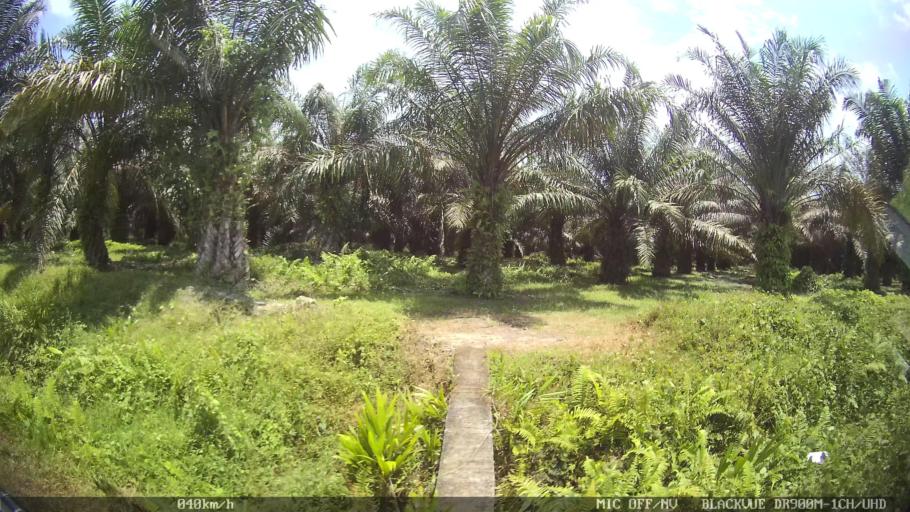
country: ID
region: North Sumatra
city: Percut
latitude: 3.5371
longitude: 98.8652
